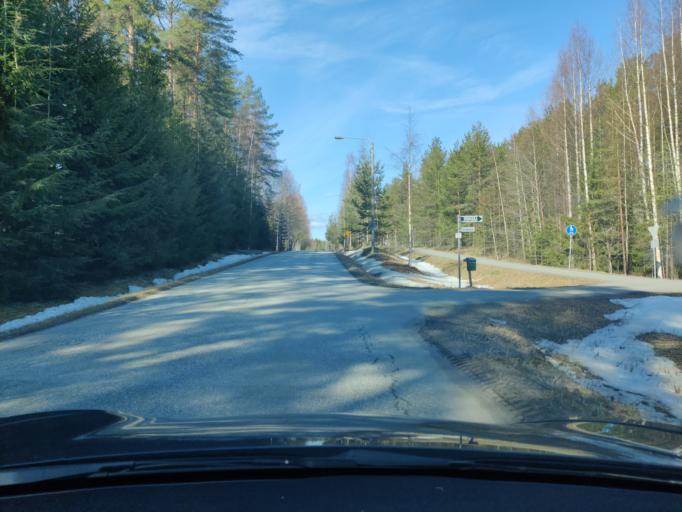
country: FI
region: Northern Savo
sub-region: Kuopio
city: Vehmersalmi
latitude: 62.7677
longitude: 27.9965
